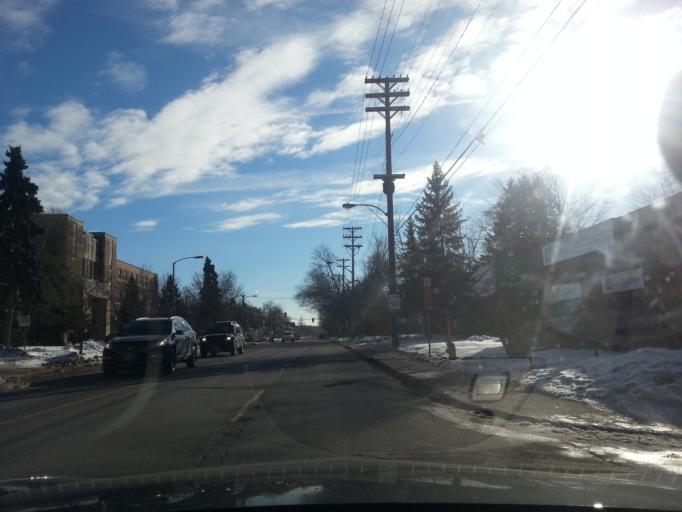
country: CA
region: Ontario
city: Ottawa
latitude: 45.4074
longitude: -75.6771
